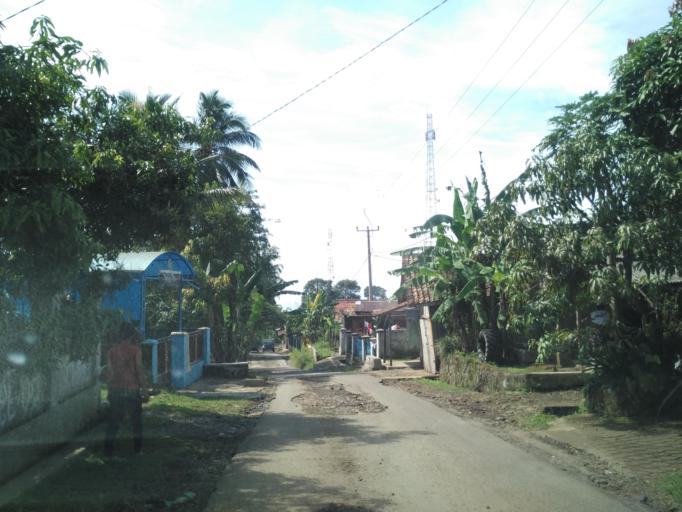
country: ID
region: West Java
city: Cibeber
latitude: -6.8389
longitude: 107.0803
